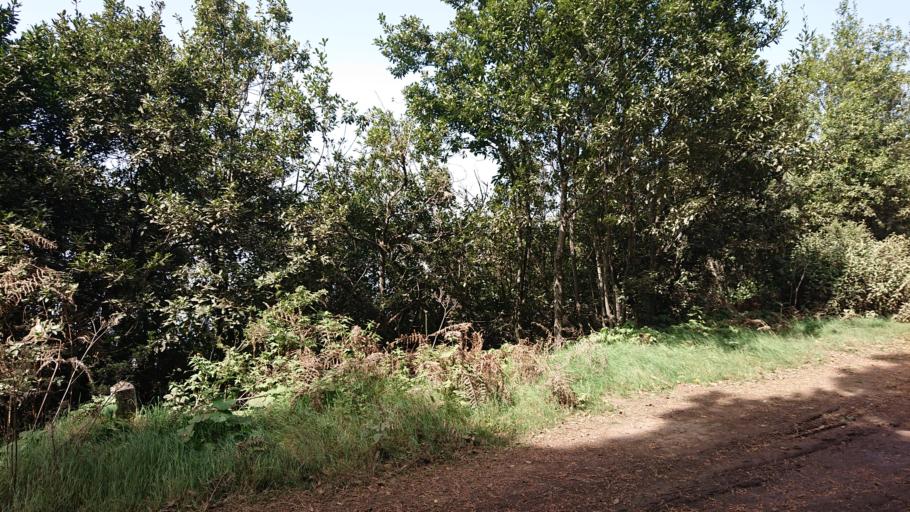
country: ES
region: Canary Islands
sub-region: Provincia de Santa Cruz de Tenerife
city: Brena Baja
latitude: 28.6443
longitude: -17.8248
